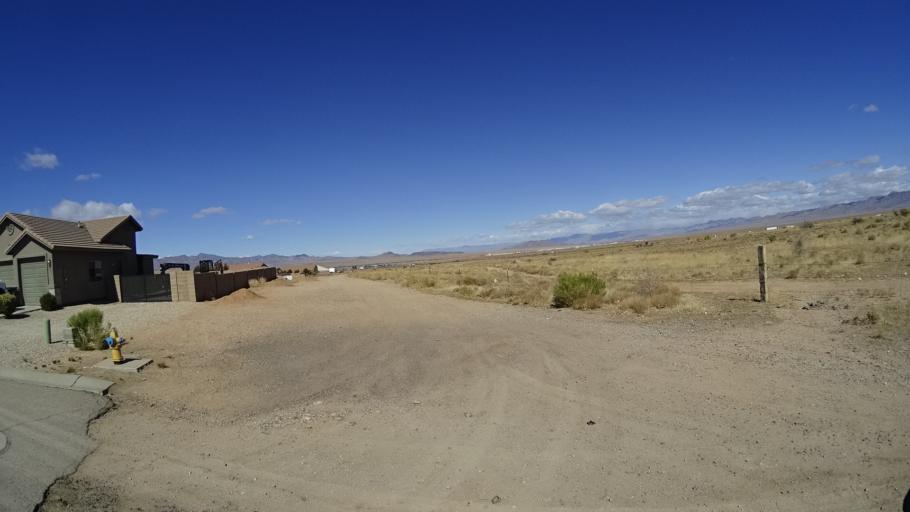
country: US
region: Arizona
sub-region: Mohave County
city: Kingman
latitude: 35.2055
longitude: -113.9676
